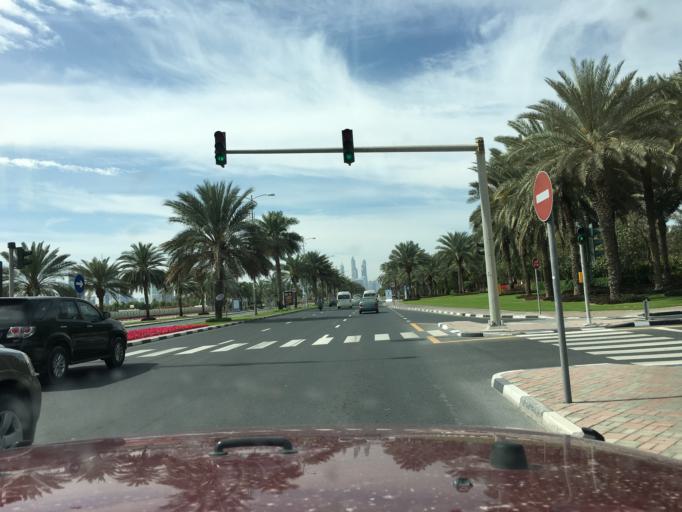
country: AE
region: Dubai
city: Dubai
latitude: 25.1304
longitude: 55.1862
